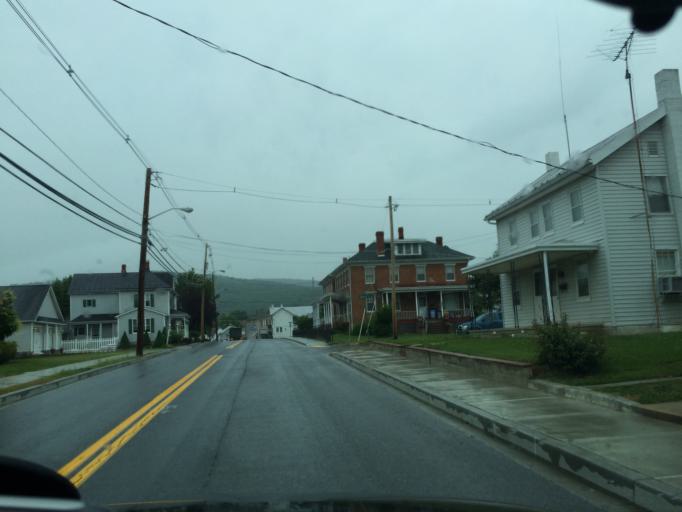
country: US
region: Maryland
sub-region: Frederick County
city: Thurmont
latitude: 39.6220
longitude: -77.4058
